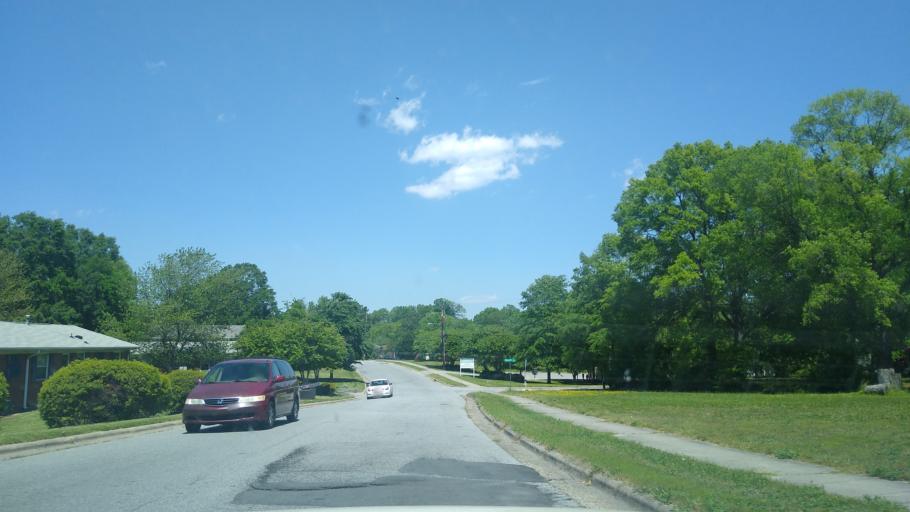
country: US
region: North Carolina
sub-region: Guilford County
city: Greensboro
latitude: 36.0687
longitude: -79.7647
